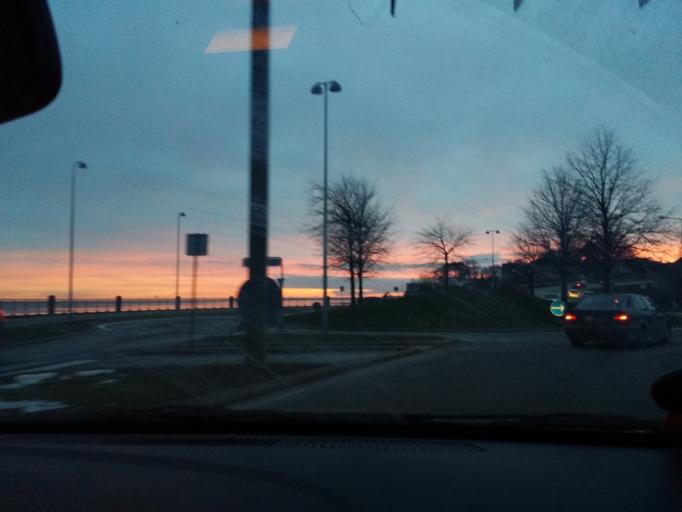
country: DK
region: Capital Region
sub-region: Helsingor Kommune
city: Helsingor
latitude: 56.0287
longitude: 12.6086
